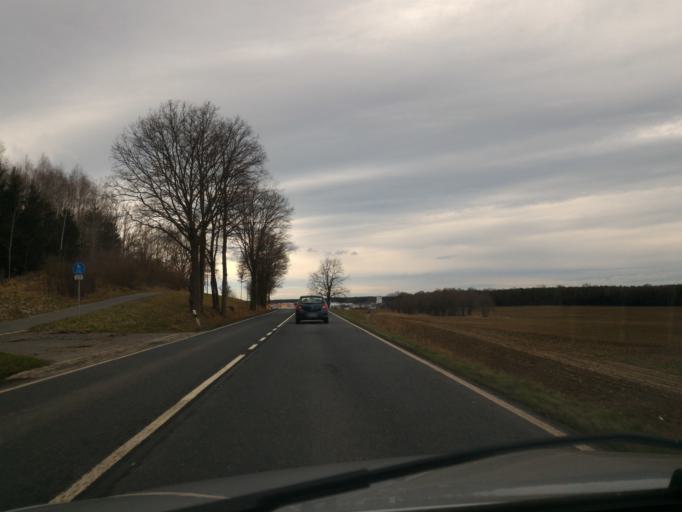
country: DE
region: Saxony
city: Radeberg
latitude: 51.0624
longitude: 13.9101
